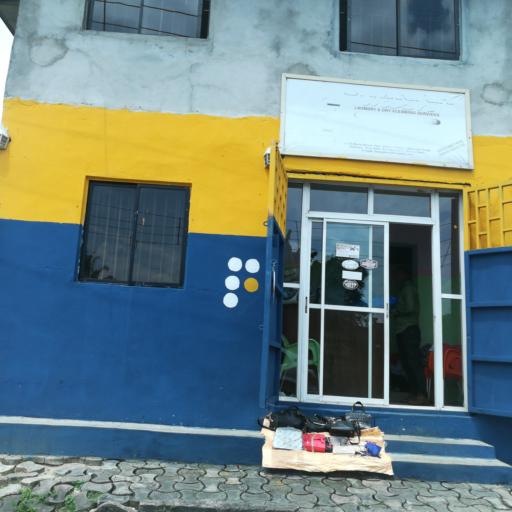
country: NG
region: Rivers
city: Port Harcourt
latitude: 4.7824
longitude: 7.0371
